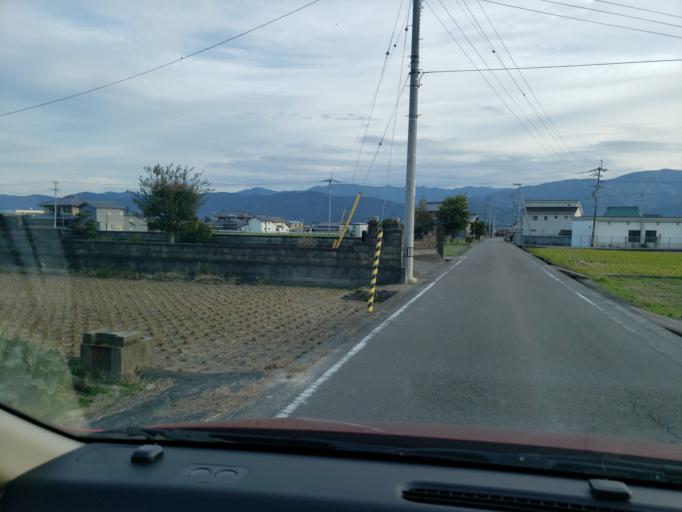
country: JP
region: Tokushima
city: Wakimachi
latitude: 34.0912
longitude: 134.2259
